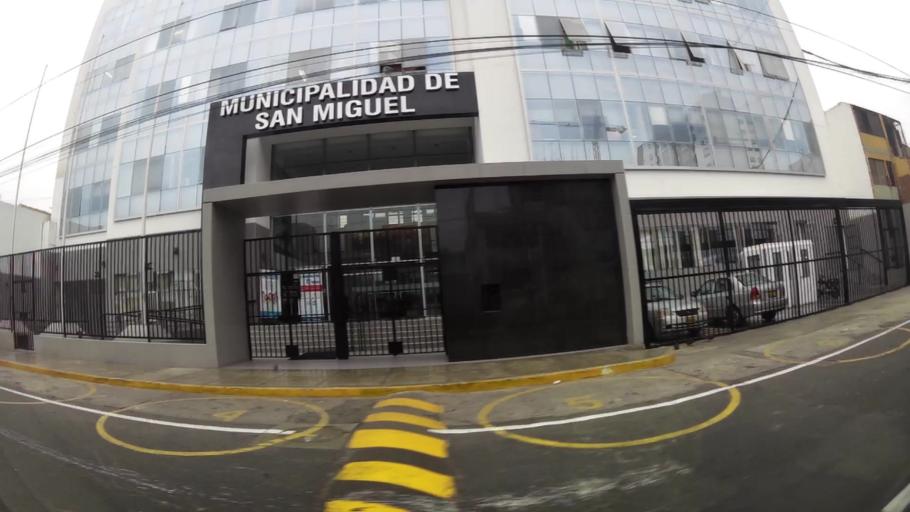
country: PE
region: Lima
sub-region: Lima
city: San Isidro
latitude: -12.0924
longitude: -77.0792
